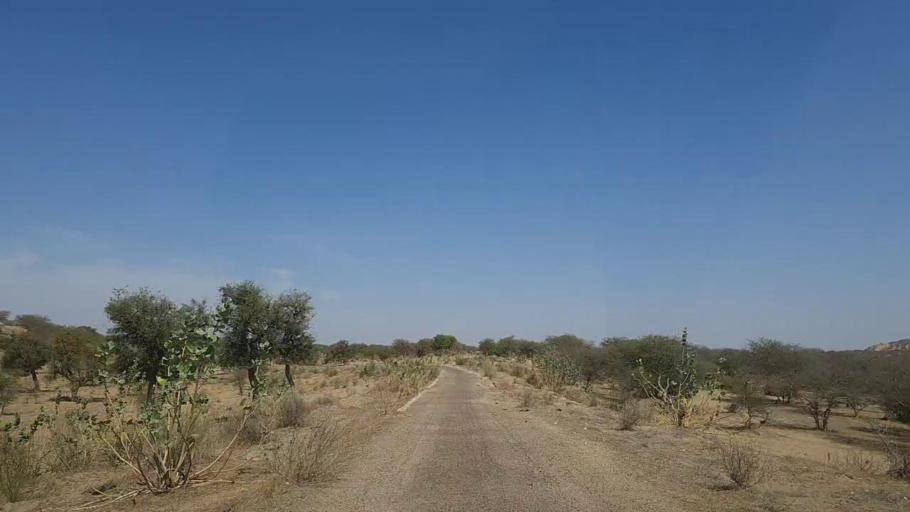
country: PK
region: Sindh
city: Mithi
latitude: 24.8609
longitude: 69.6604
